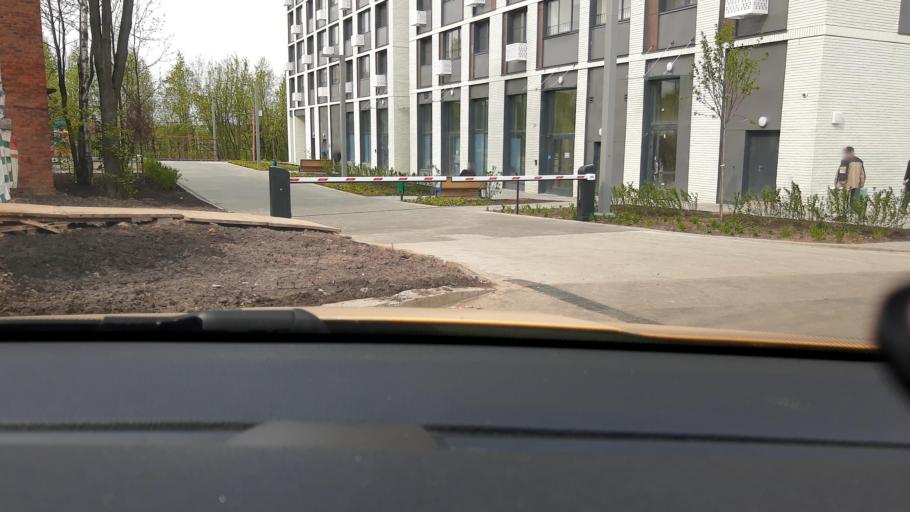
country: RU
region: Moskovskaya
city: Pavshino
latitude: 55.8511
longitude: 37.3792
